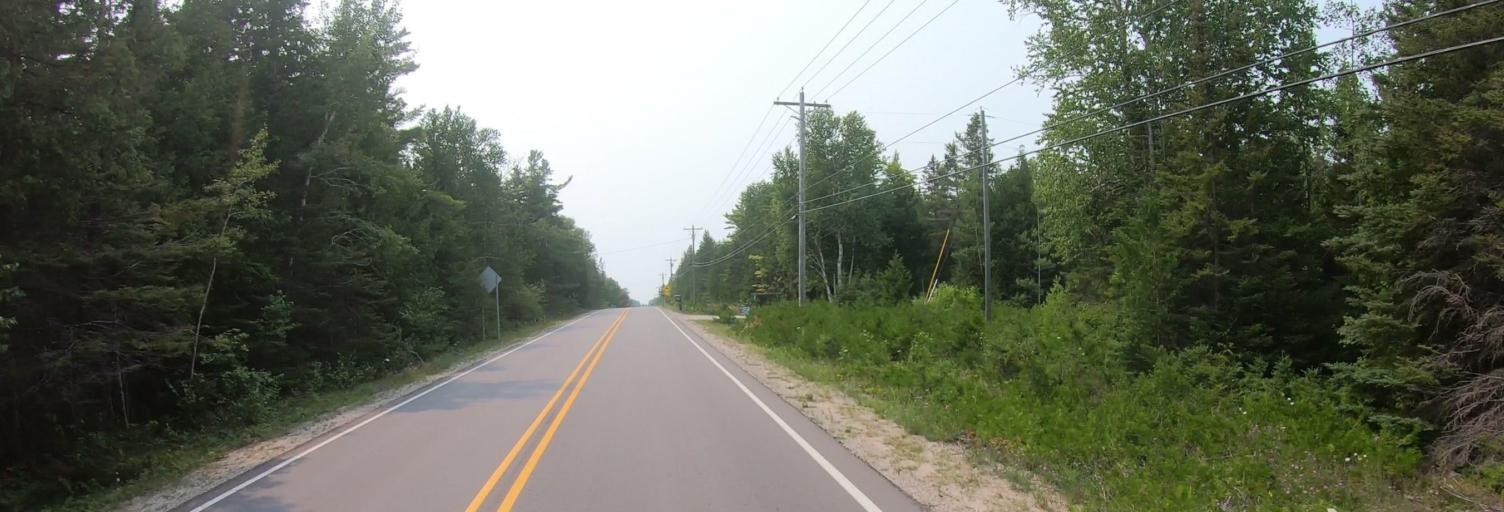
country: CA
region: Ontario
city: Thessalon
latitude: 45.9996
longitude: -83.9093
